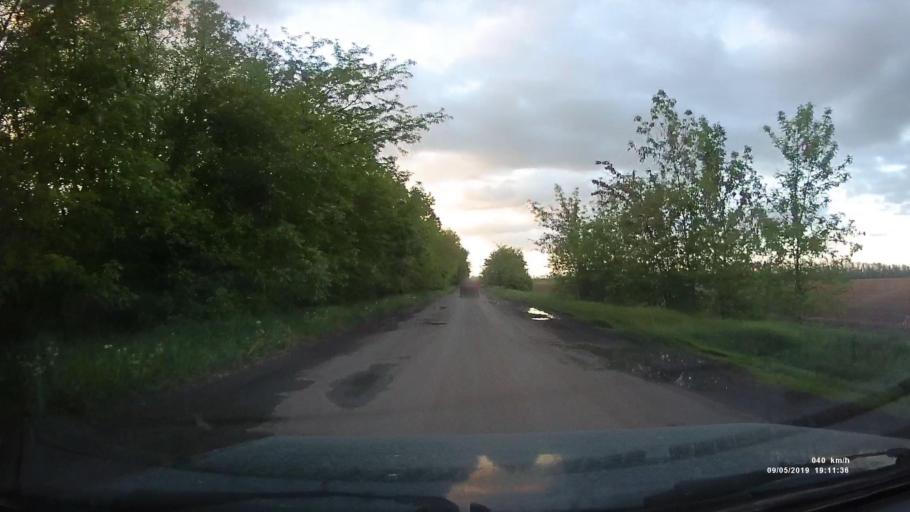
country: RU
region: Krasnodarskiy
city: Kanelovskaya
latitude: 46.7363
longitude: 39.2136
